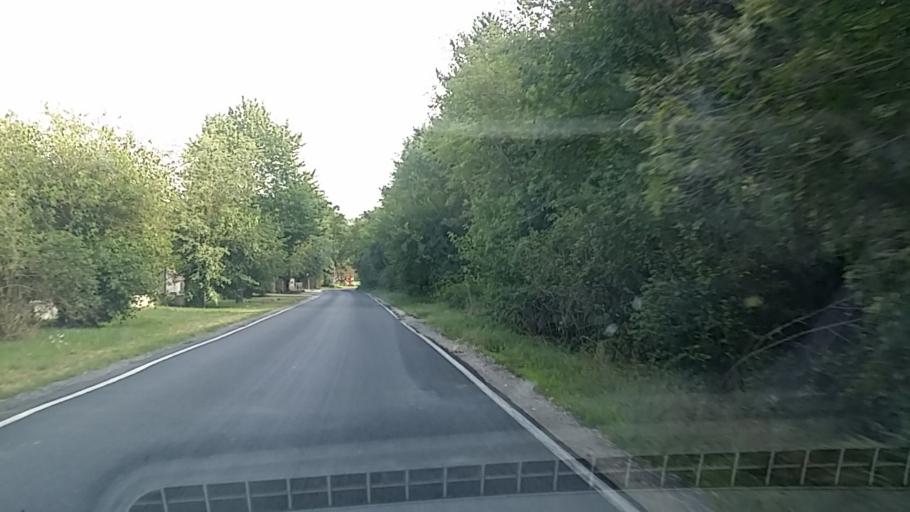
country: HU
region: Gyor-Moson-Sopron
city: Fertorakos
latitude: 47.7282
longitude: 16.6226
